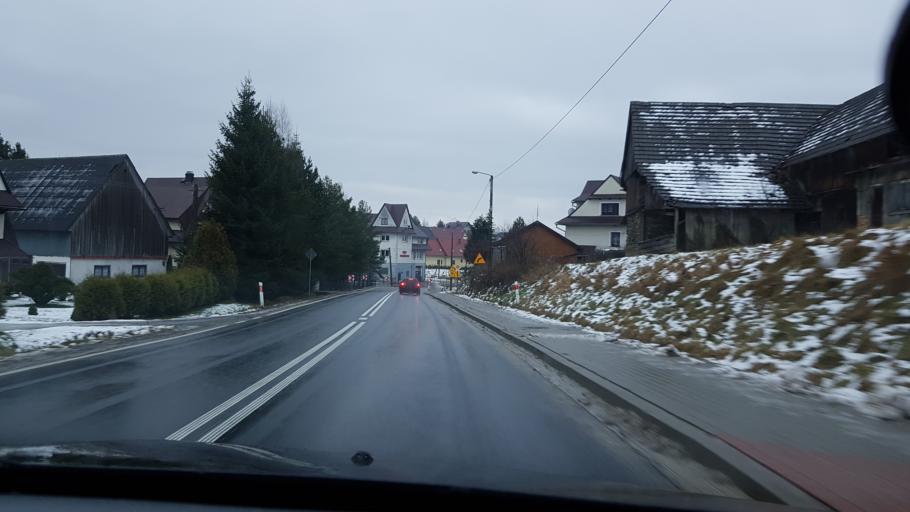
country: PL
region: Lesser Poland Voivodeship
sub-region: Powiat nowotarski
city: Sieniawa
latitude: 49.5047
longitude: 19.8884
